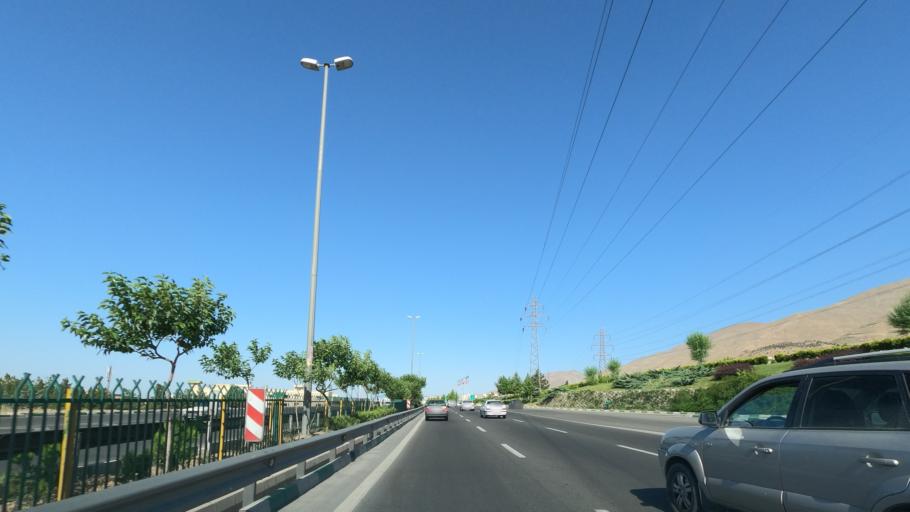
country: IR
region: Tehran
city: Shahr-e Qods
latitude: 35.7607
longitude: 51.2480
